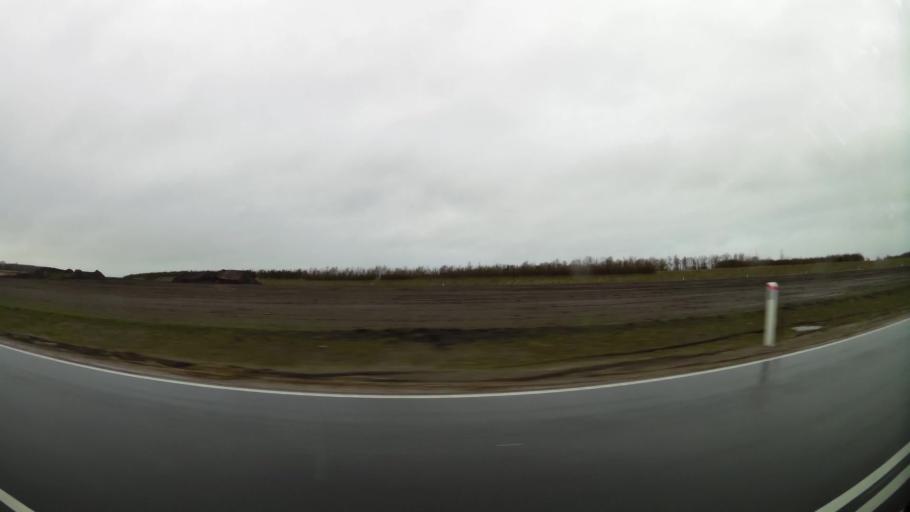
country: DK
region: Central Jutland
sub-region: Herning Kommune
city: Snejbjerg
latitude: 56.1915
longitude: 8.8934
